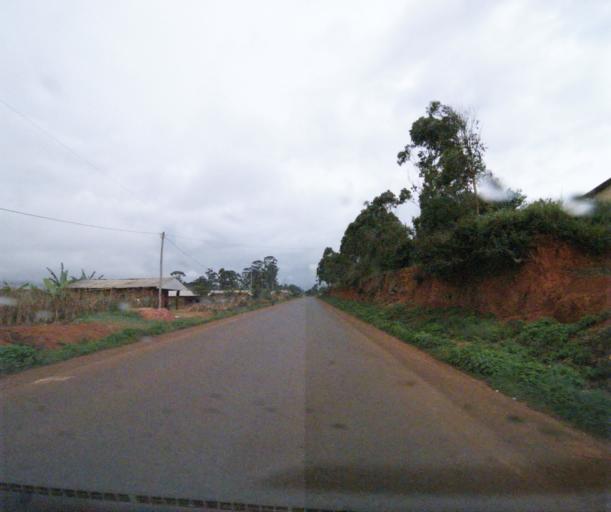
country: CM
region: West
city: Dschang
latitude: 5.4893
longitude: 10.1731
